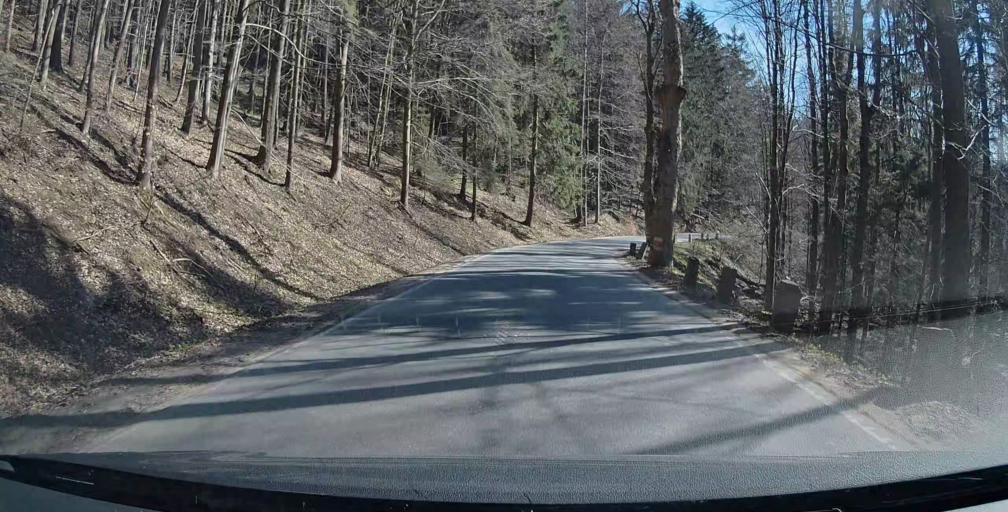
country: CZ
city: Machov
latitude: 50.4556
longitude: 16.2971
